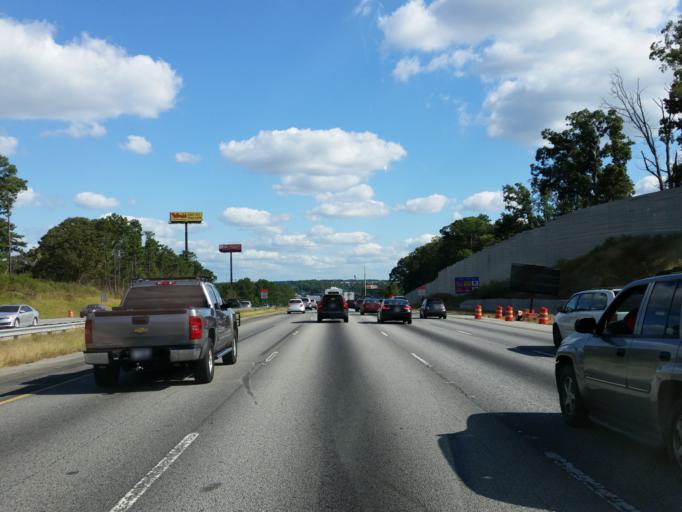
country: US
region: Georgia
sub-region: Henry County
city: Stockbridge
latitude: 33.5225
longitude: -84.2500
